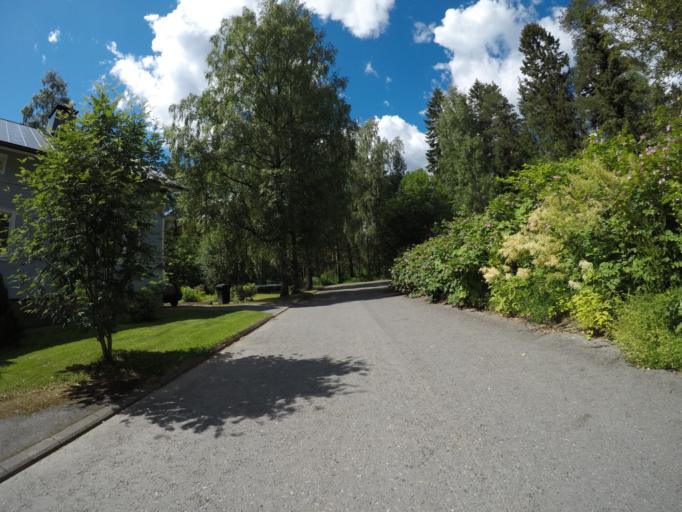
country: FI
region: Haeme
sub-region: Haemeenlinna
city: Haemeenlinna
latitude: 61.0127
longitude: 24.4347
